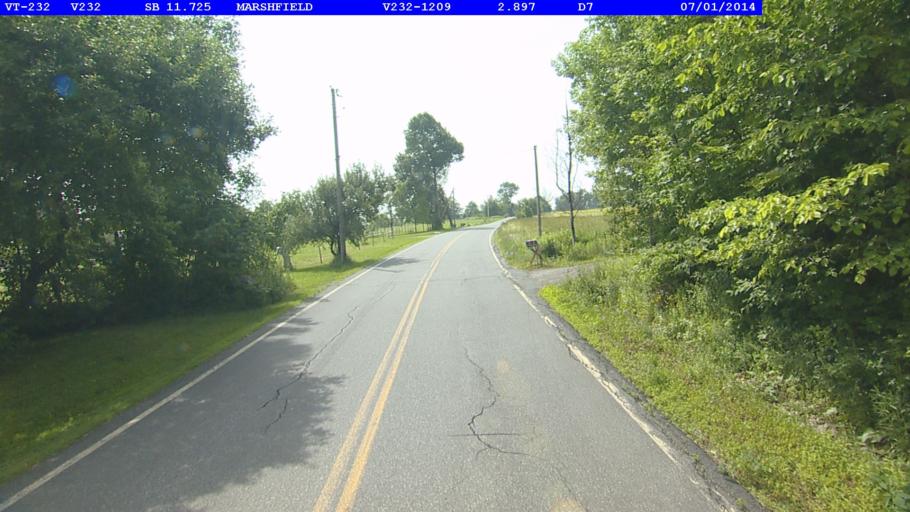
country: US
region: Vermont
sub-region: Caledonia County
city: Hardwick
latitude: 44.3481
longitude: -72.2999
